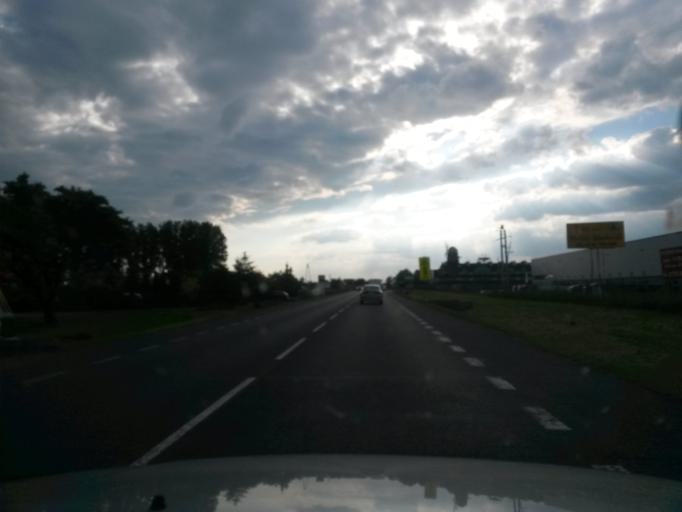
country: PL
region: Lodz Voivodeship
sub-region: Powiat piotrkowski
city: Wola Krzysztoporska
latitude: 51.4144
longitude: 19.5892
